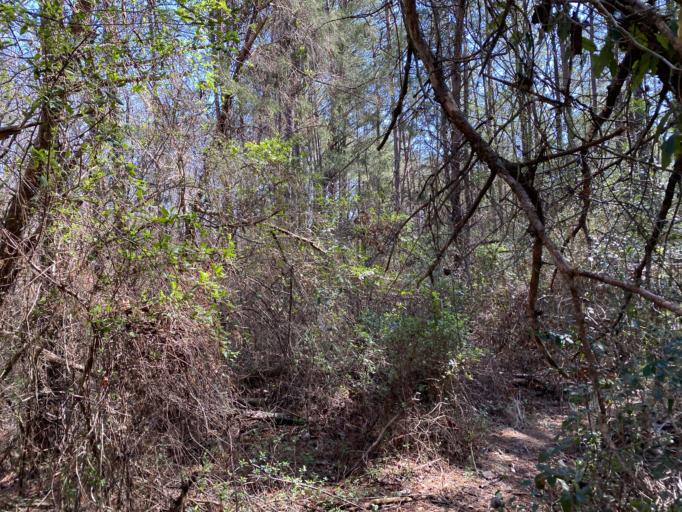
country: US
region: Georgia
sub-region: Gordon County
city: Calhoun
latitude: 34.4638
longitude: -84.9867
